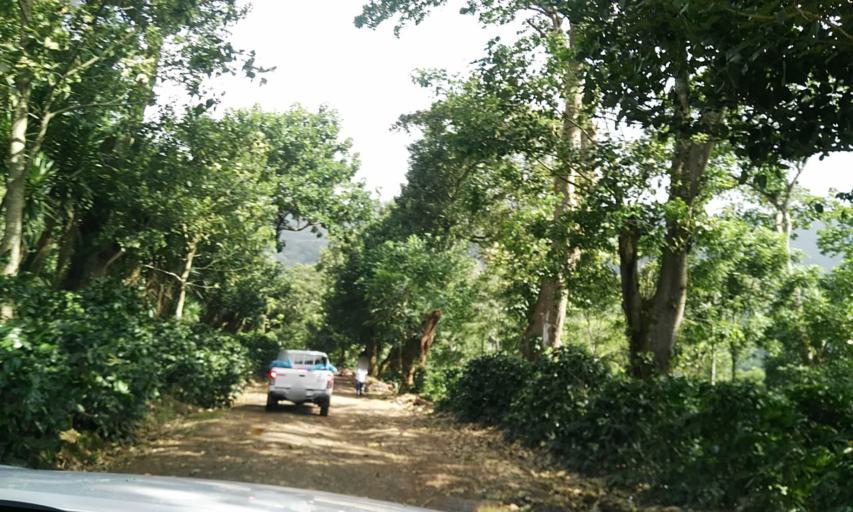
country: NI
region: Matagalpa
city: San Ramon
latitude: 13.0037
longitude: -85.8707
